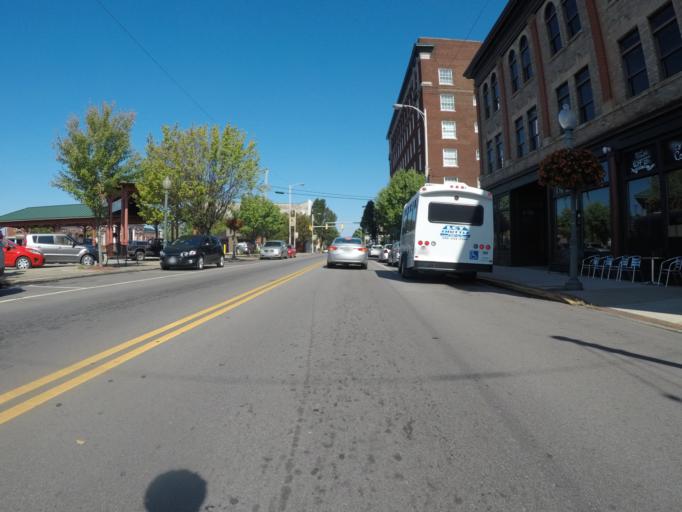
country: US
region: Ohio
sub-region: Lawrence County
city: Ironton
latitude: 38.5336
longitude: -82.6851
